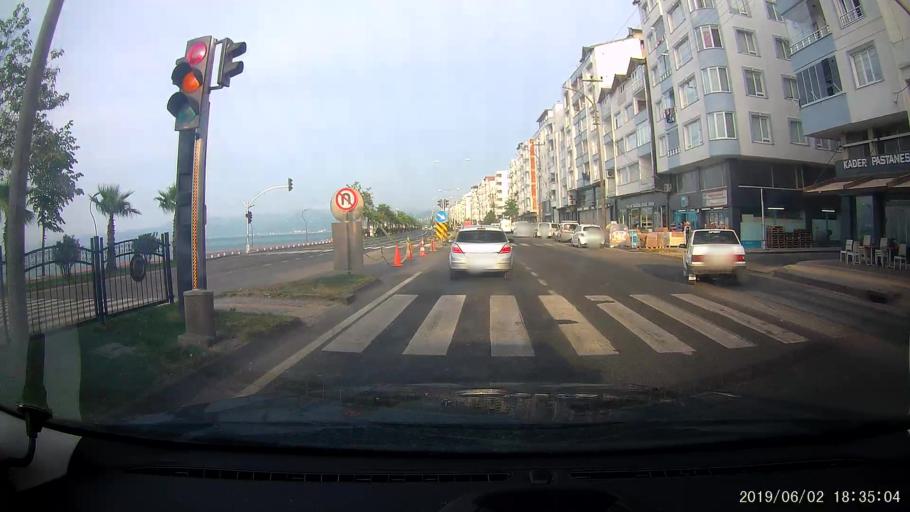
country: TR
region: Ordu
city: Fatsa
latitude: 41.0274
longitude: 37.5103
